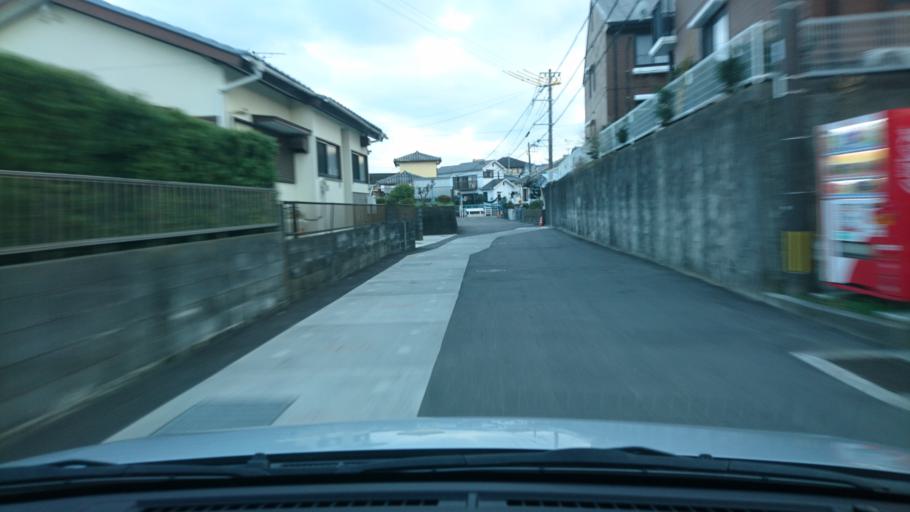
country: JP
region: Miyazaki
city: Miyazaki-shi
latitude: 31.8590
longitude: 131.4309
